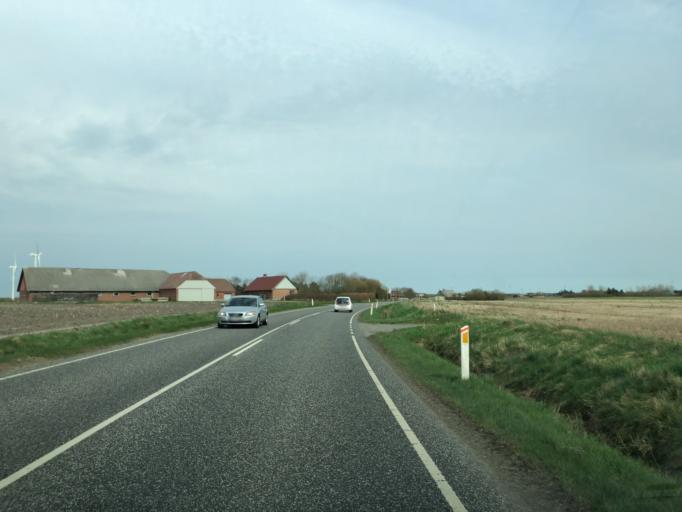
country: DK
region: Central Jutland
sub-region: Ringkobing-Skjern Kommune
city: Skjern
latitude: 55.8362
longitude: 8.3225
